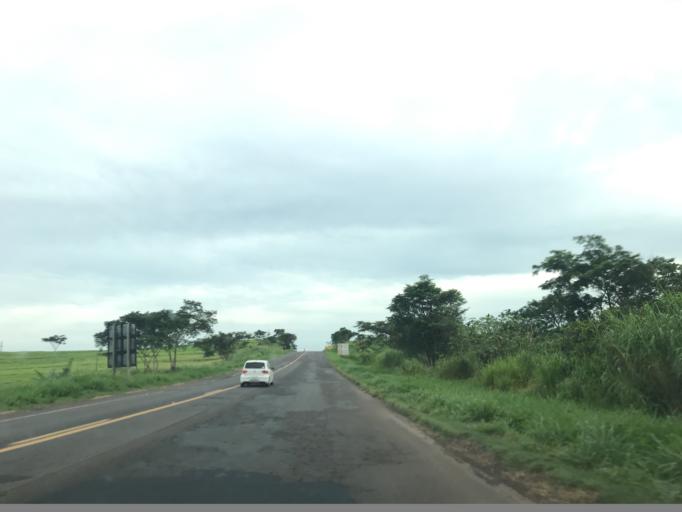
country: BR
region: Sao Paulo
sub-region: Birigui
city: Birigui
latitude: -21.5778
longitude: -50.4497
